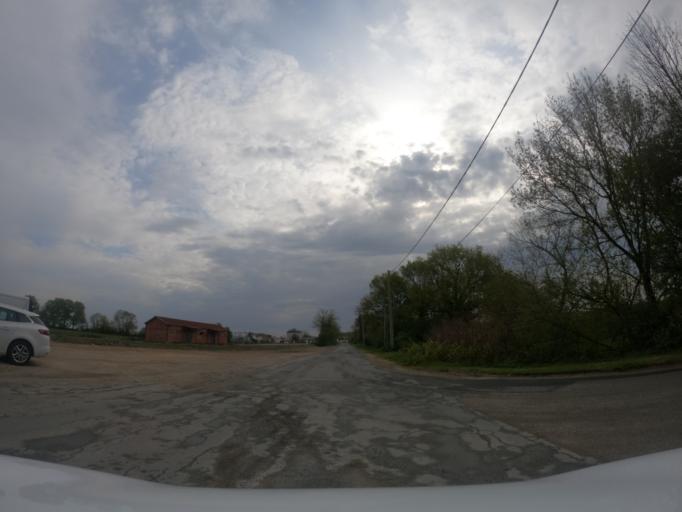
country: FR
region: Pays de la Loire
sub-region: Departement de la Vendee
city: Le Champ-Saint-Pere
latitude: 46.5132
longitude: -1.3447
